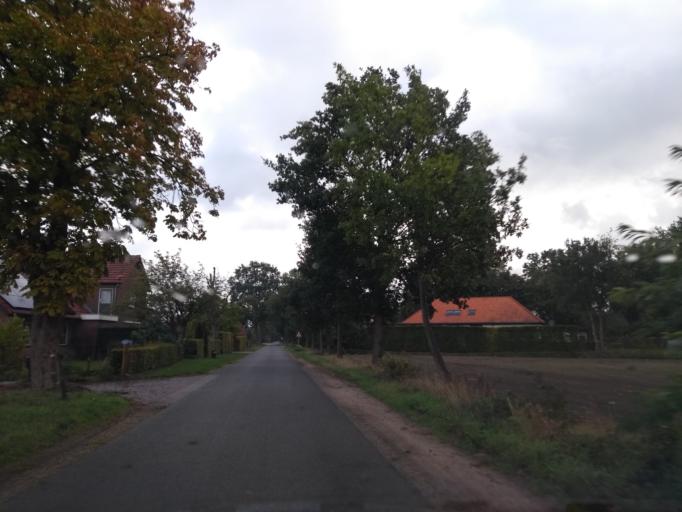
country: NL
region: Gelderland
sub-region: Gemeente Bronckhorst
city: Zelhem
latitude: 52.0130
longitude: 6.3847
